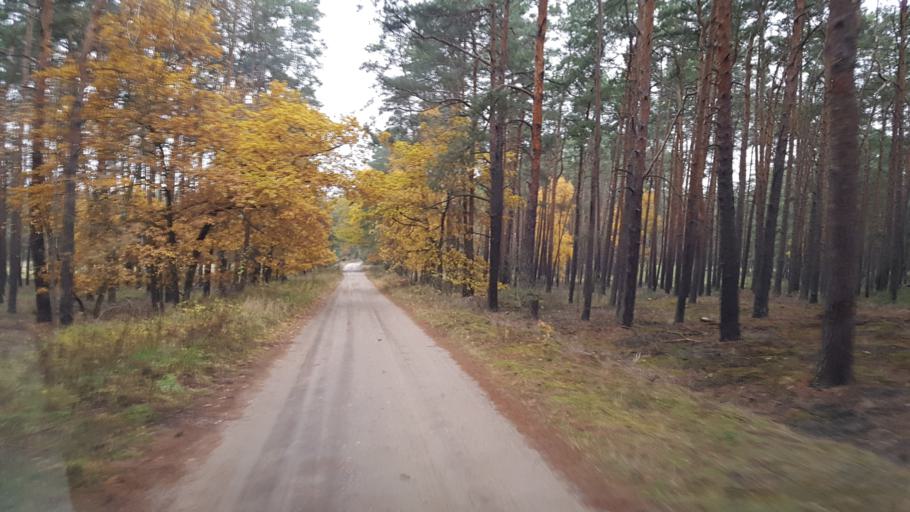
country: DE
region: Brandenburg
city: Schilda
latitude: 51.6496
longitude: 13.3846
